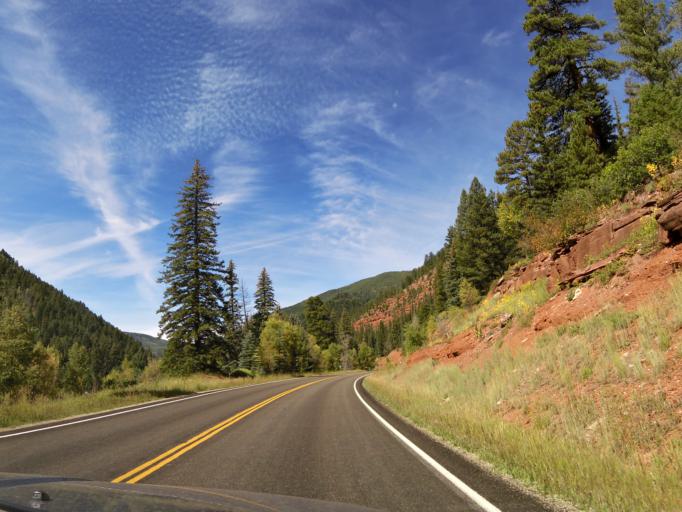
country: US
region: Colorado
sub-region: Montezuma County
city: Mancos
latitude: 37.5879
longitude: -108.1508
